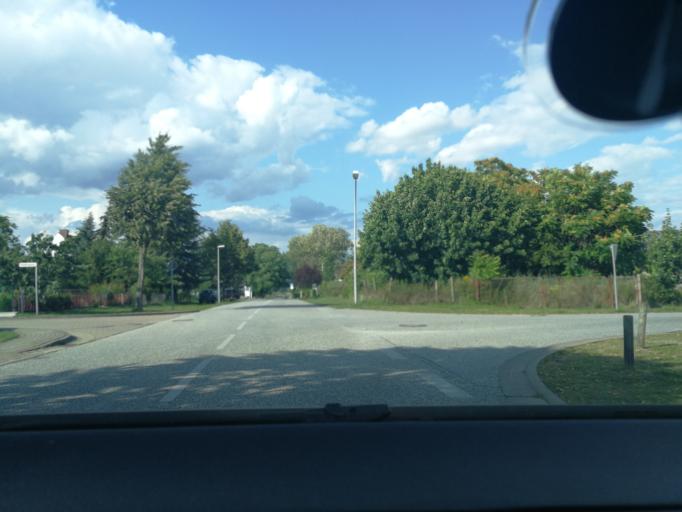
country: DE
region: Brandenburg
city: Pritzwalk
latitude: 53.1598
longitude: 12.1816
